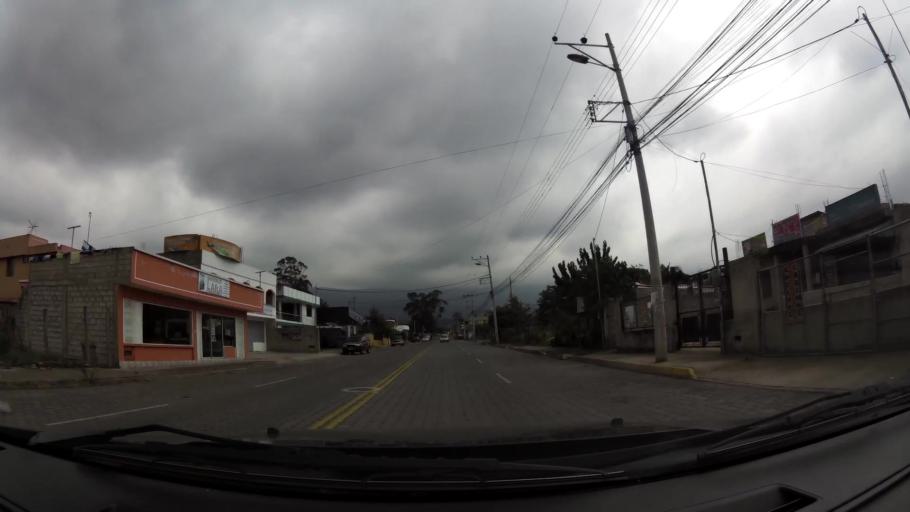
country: EC
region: Pichincha
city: Sangolqui
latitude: -0.3267
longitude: -78.4752
